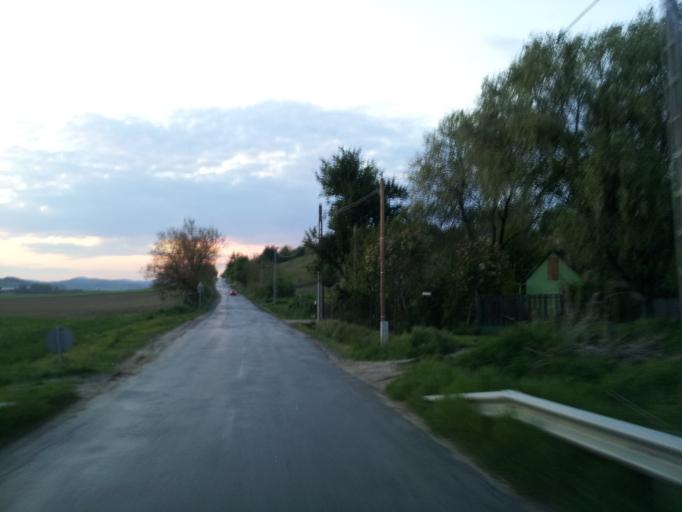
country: HU
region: Pest
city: Perbal
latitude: 47.6358
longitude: 18.7312
